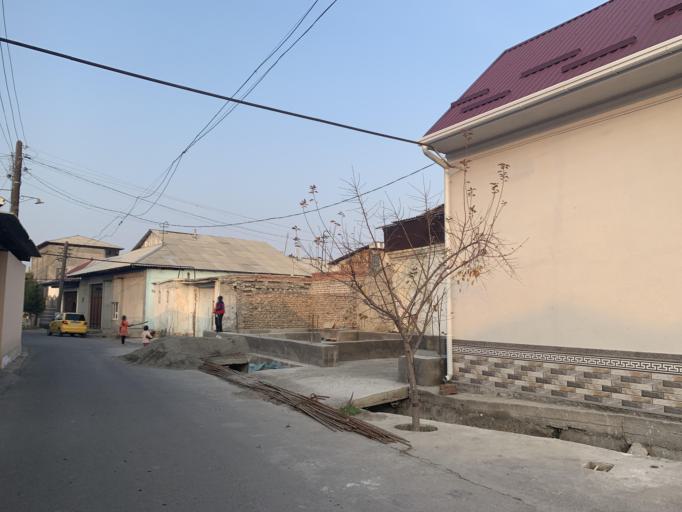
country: UZ
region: Fergana
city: Qo`qon
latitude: 40.5340
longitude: 70.9309
